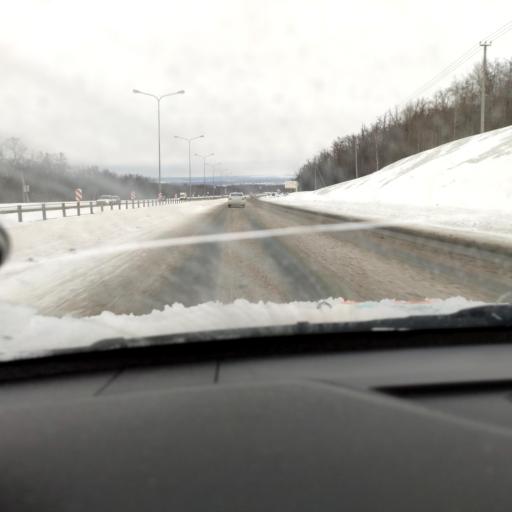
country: RU
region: Samara
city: Novosemeykino
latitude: 53.3746
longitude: 50.3113
